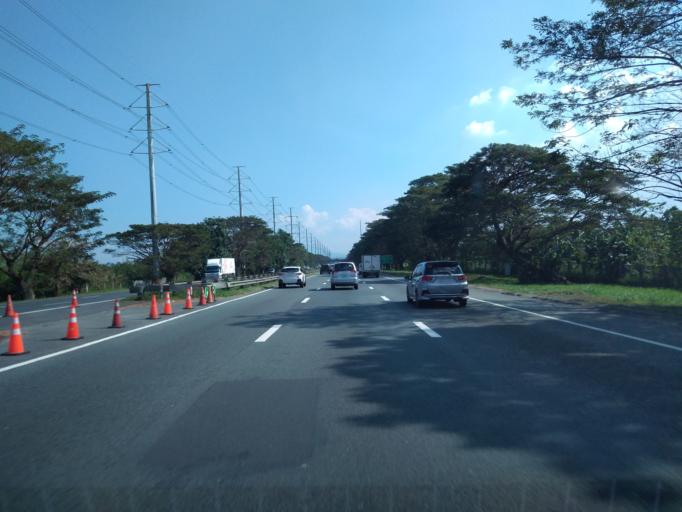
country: PH
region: Calabarzon
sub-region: Province of Laguna
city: Pulong Santa Cruz
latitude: 14.2637
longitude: 121.0993
